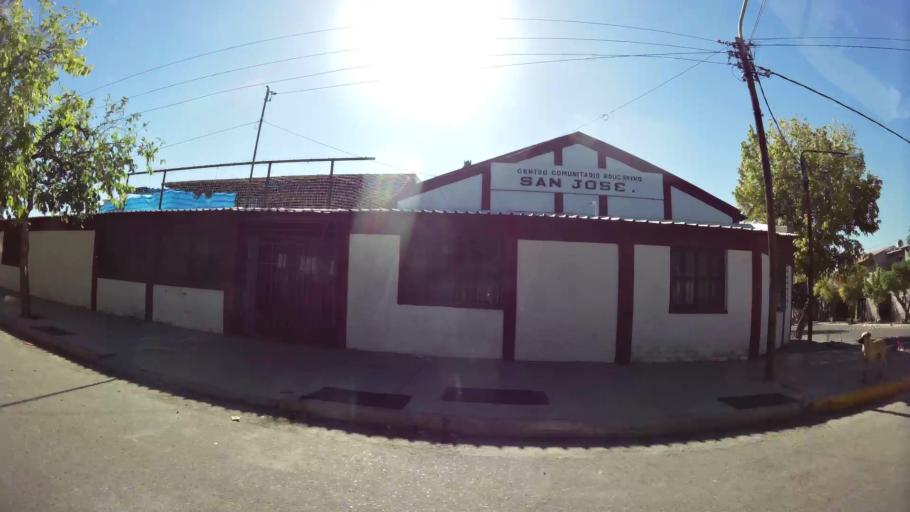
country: AR
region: Mendoza
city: Mendoza
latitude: -32.8742
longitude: -68.8702
